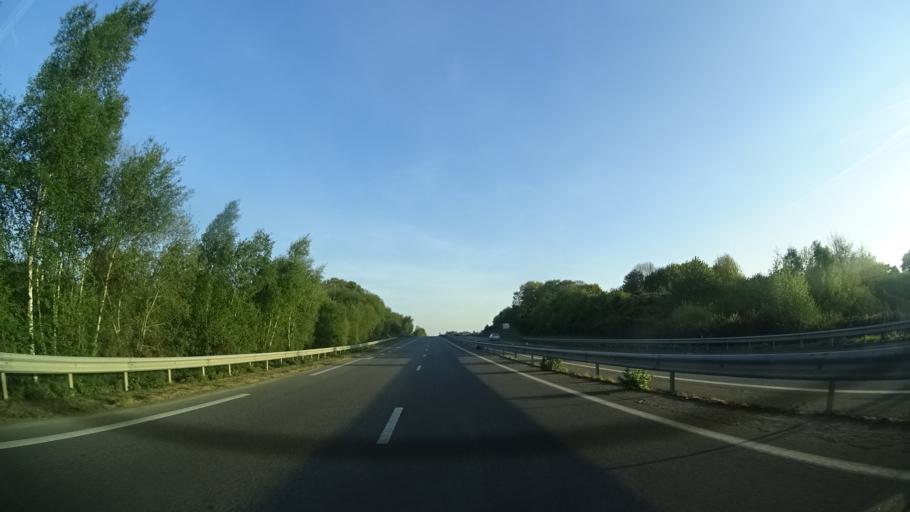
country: FR
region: Brittany
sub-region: Departement d'Ille-et-Vilaine
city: Guichen
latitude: 47.9782
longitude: -1.8144
